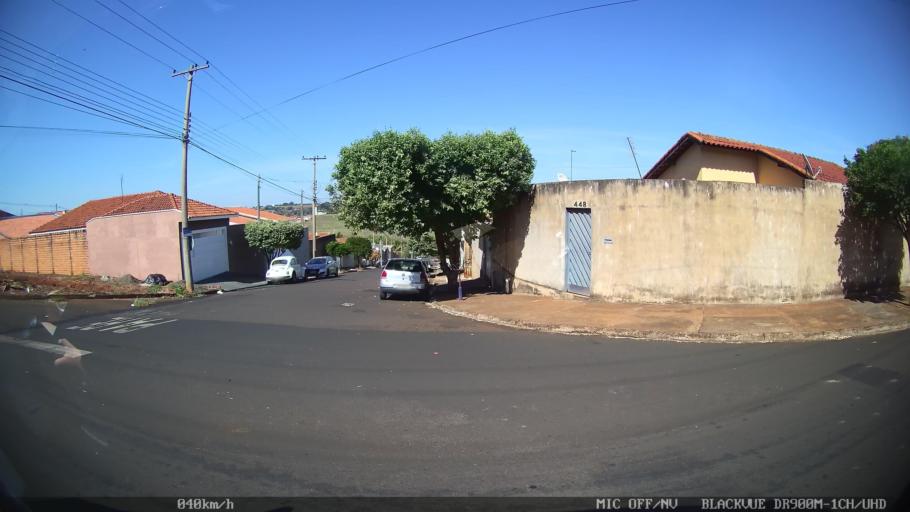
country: BR
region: Sao Paulo
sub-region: Batatais
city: Batatais
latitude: -20.8887
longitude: -47.5670
